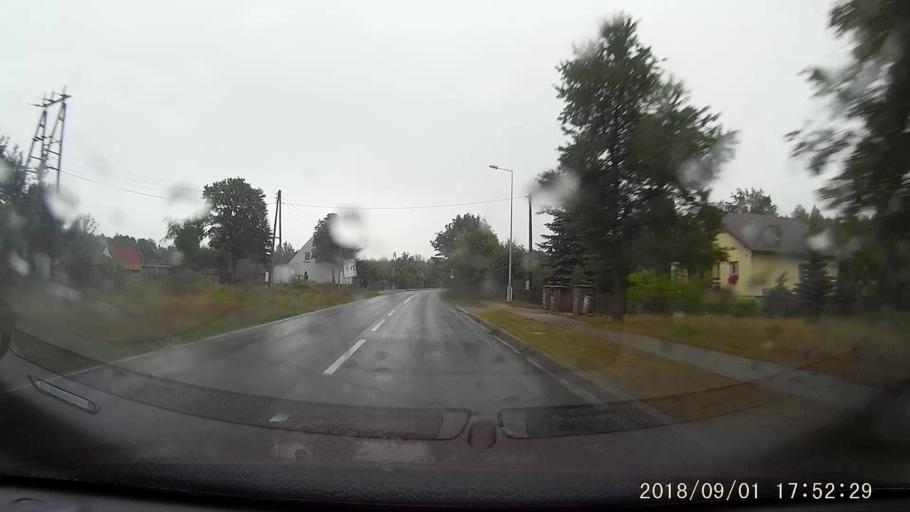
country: PL
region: Lubusz
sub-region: Powiat zaganski
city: Ilowa
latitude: 51.4891
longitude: 15.1942
